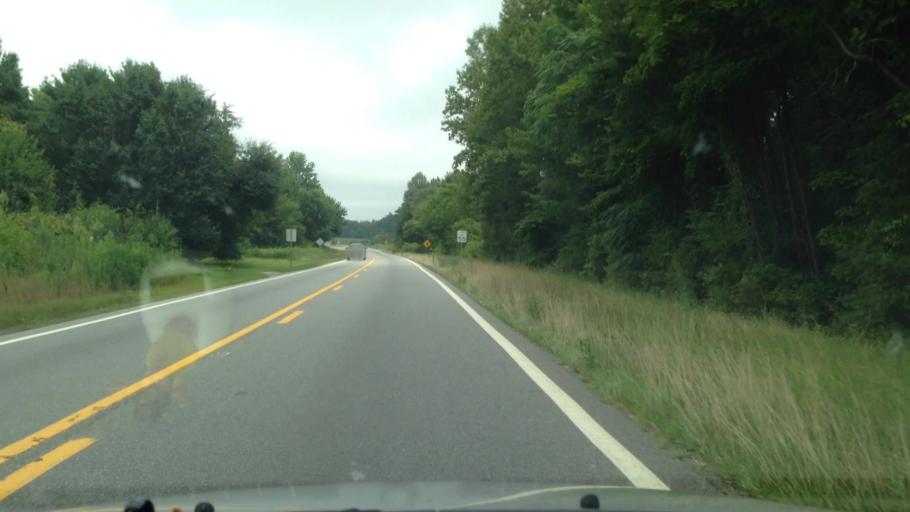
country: US
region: North Carolina
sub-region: Guilford County
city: Stokesdale
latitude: 36.2764
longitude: -79.9426
